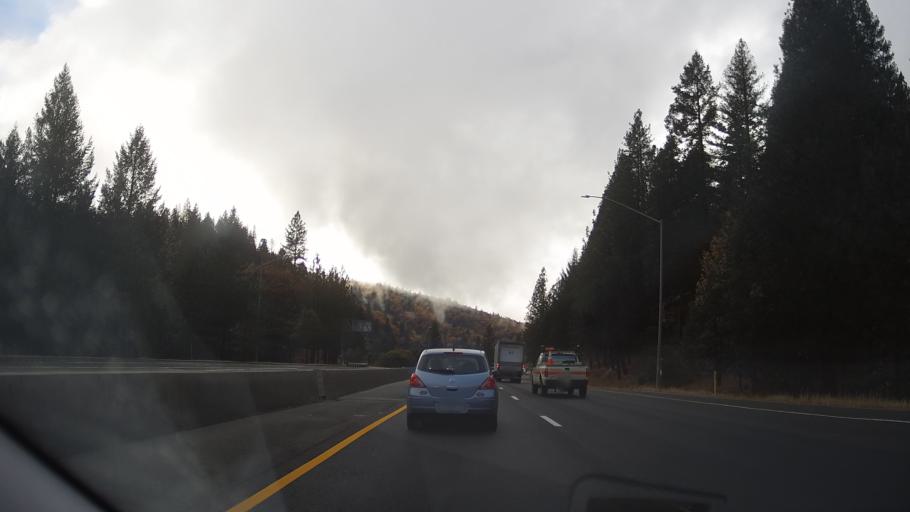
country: US
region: California
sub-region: Placer County
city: Colfax
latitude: 39.2003
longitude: -120.8143
